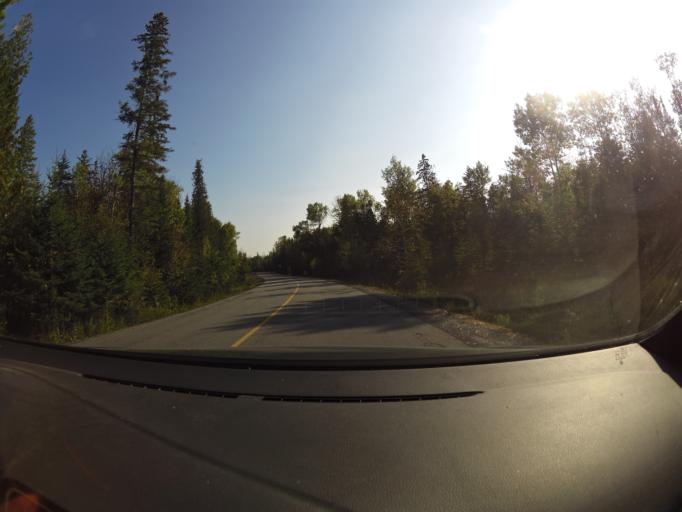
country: CA
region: Ontario
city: Arnprior
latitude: 45.4474
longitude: -76.2780
